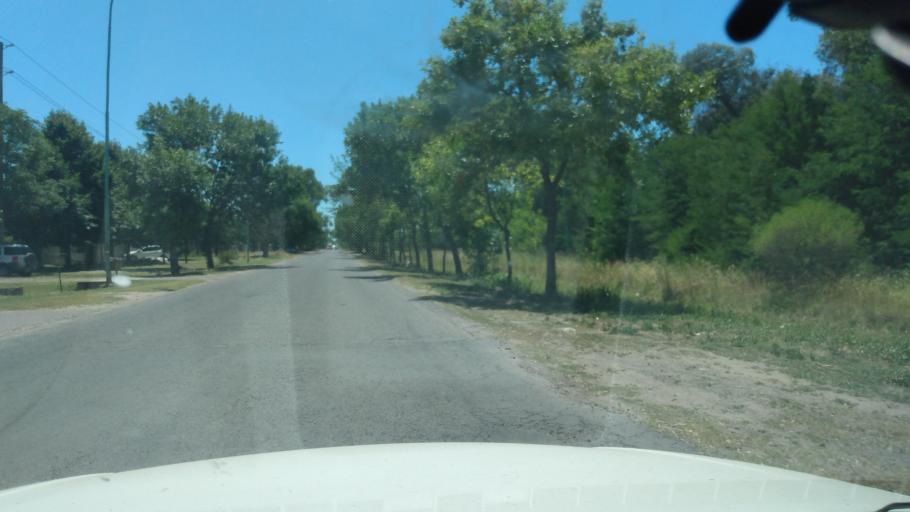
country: AR
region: Buenos Aires
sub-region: Partido de Lujan
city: Lujan
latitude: -34.5808
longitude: -59.1733
